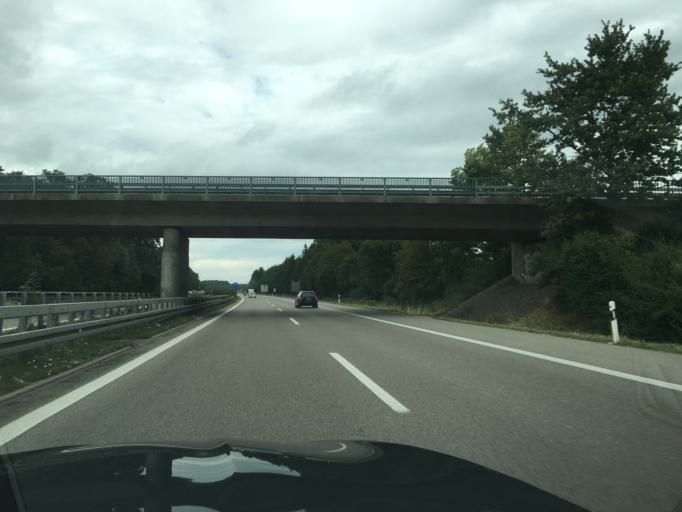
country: DE
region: Bavaria
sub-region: Swabia
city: Holzheim
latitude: 48.4010
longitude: 10.0917
